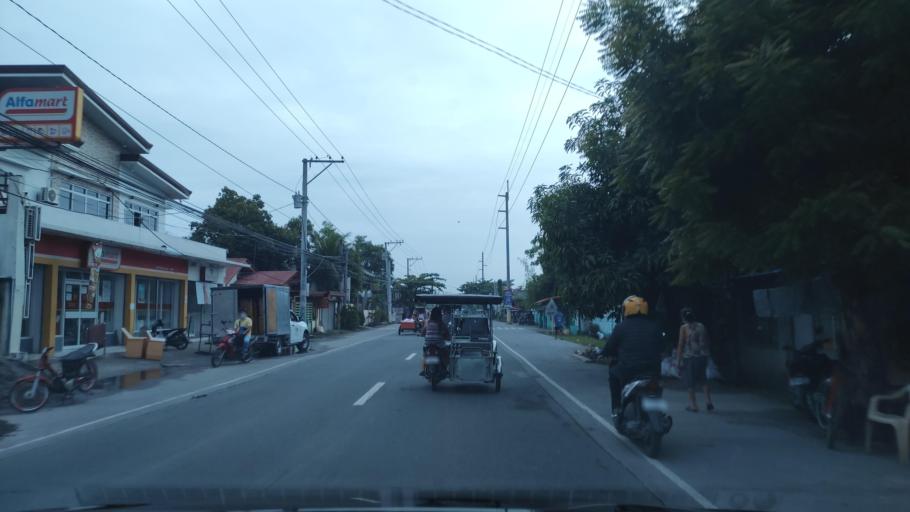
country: PH
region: Central Luzon
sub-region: Province of Pampanga
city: Santa Ana
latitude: 15.1065
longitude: 120.7713
